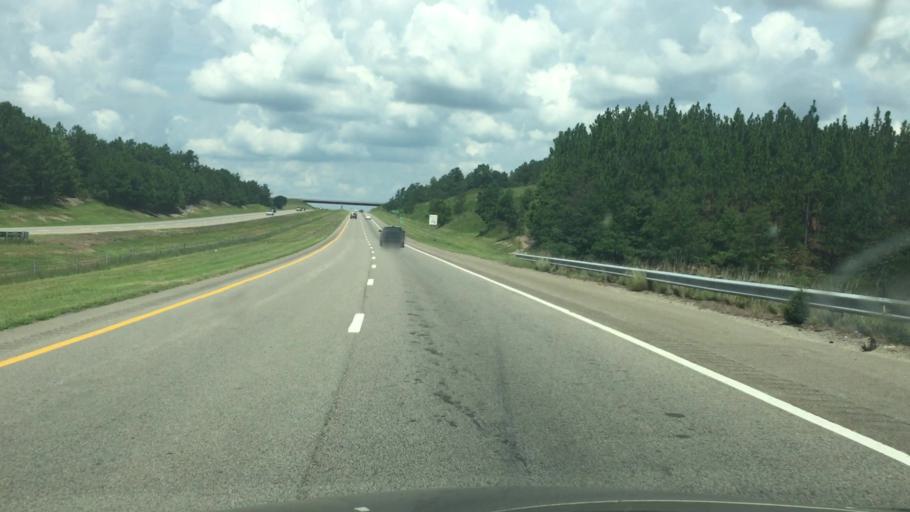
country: US
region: North Carolina
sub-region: Richmond County
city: Ellerbe
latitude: 35.1819
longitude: -79.7155
